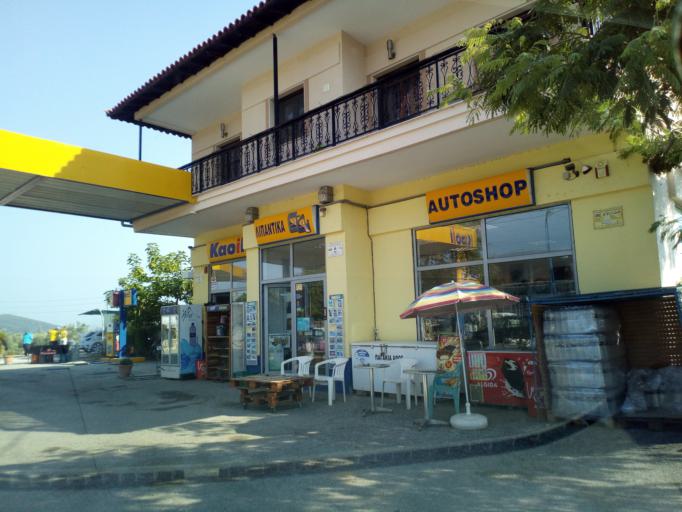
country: GR
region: Central Macedonia
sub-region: Nomos Chalkidikis
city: Ormylia
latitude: 40.2613
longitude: 23.5216
